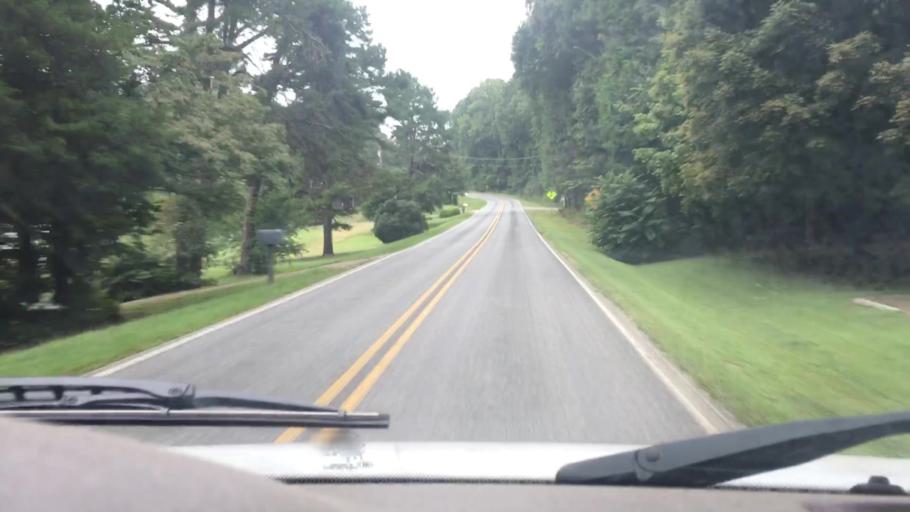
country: US
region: North Carolina
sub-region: Gaston County
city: Davidson
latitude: 35.5174
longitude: -80.8347
